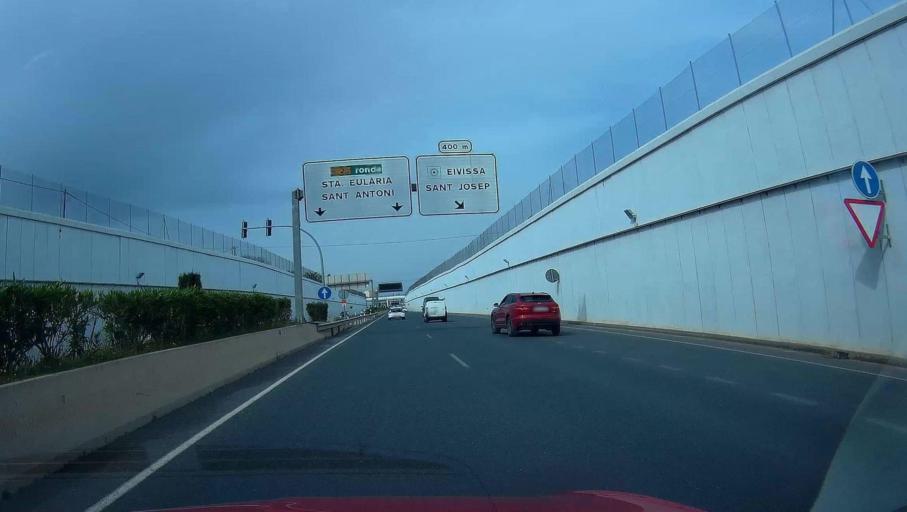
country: ES
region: Balearic Islands
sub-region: Illes Balears
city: Ibiza
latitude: 38.8979
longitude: 1.4021
